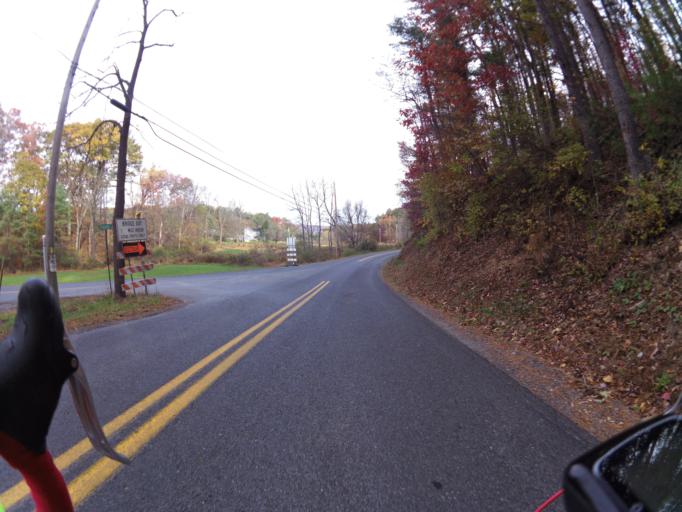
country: US
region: Pennsylvania
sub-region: Union County
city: New Columbia
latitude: 41.0380
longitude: -76.9220
